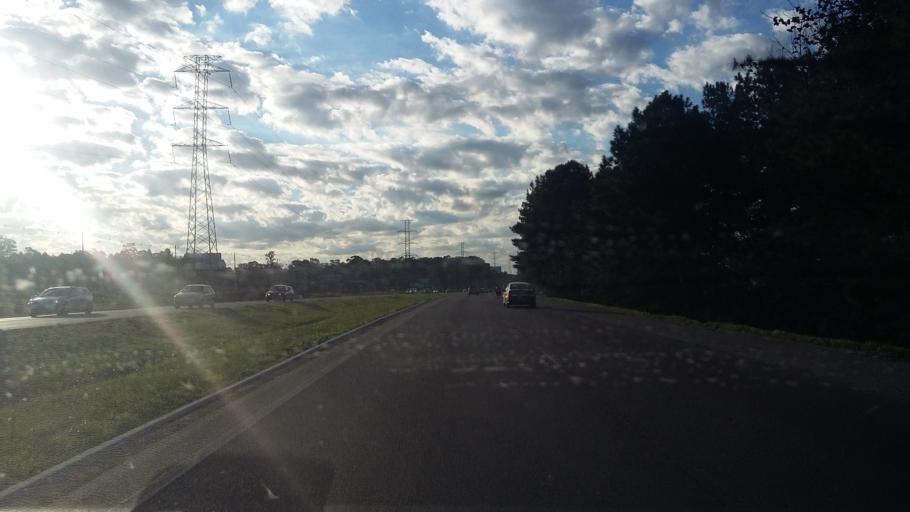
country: BR
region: Parana
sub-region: Curitiba
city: Curitiba
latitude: -25.4693
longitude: -49.3548
